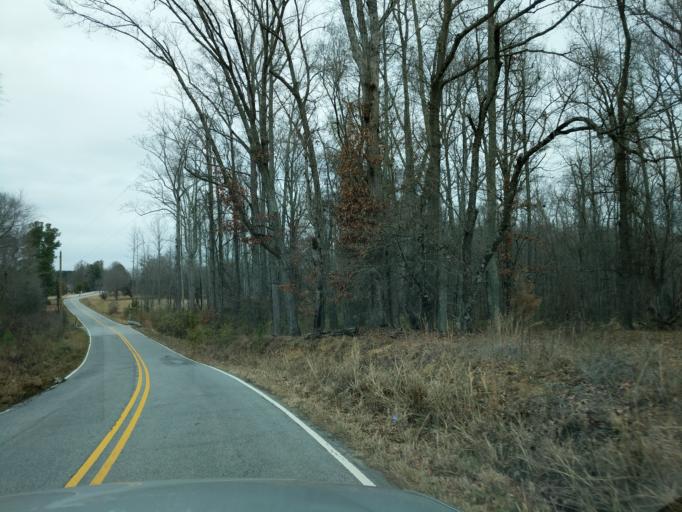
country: US
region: South Carolina
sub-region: Spartanburg County
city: Duncan
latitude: 34.8689
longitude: -82.1273
